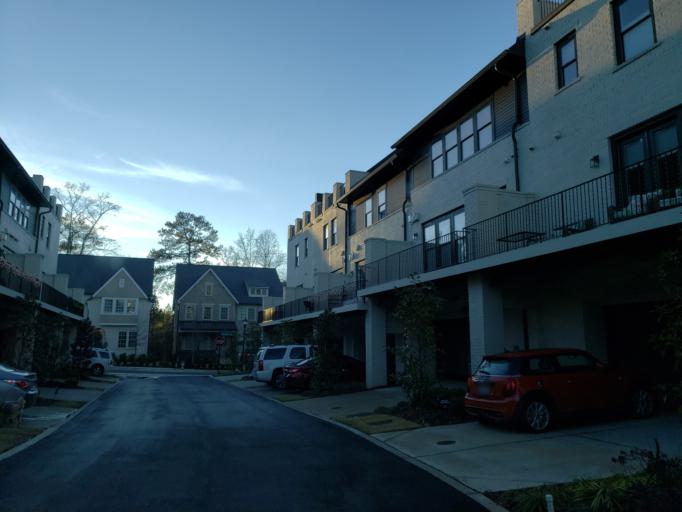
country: US
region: Georgia
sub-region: Fulton County
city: Sandy Springs
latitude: 33.9304
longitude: -84.3670
